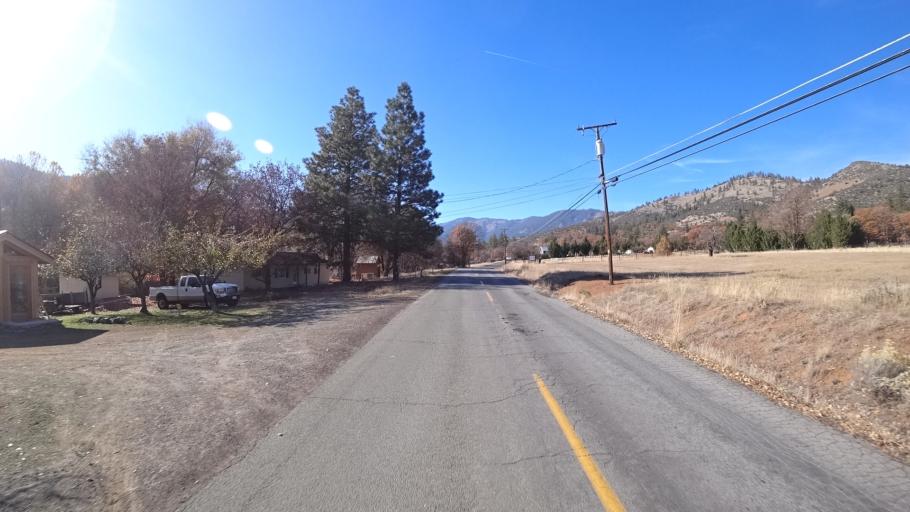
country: US
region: California
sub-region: Siskiyou County
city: Yreka
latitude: 41.7151
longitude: -122.6599
